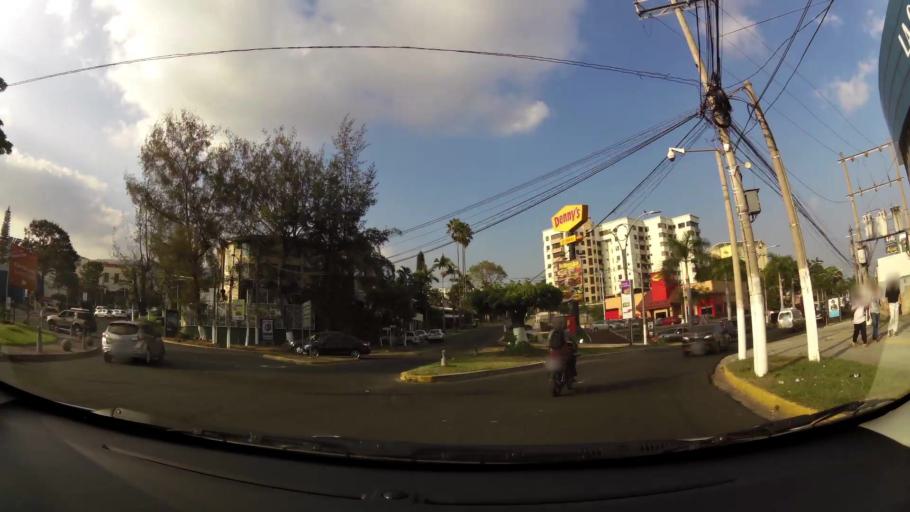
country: SV
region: La Libertad
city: Antiguo Cuscatlan
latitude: 13.6898
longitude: -89.2396
